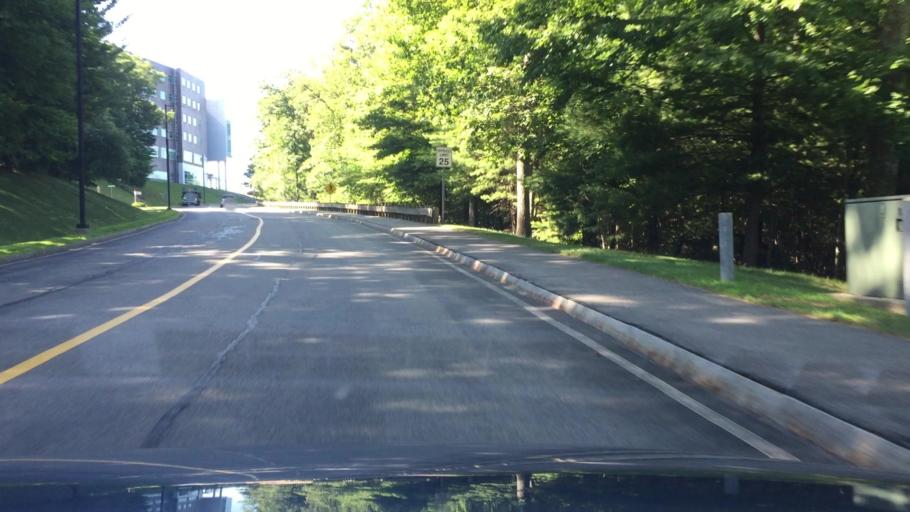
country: US
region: Massachusetts
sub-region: Middlesex County
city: Marlborough
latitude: 42.3271
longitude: -71.5857
